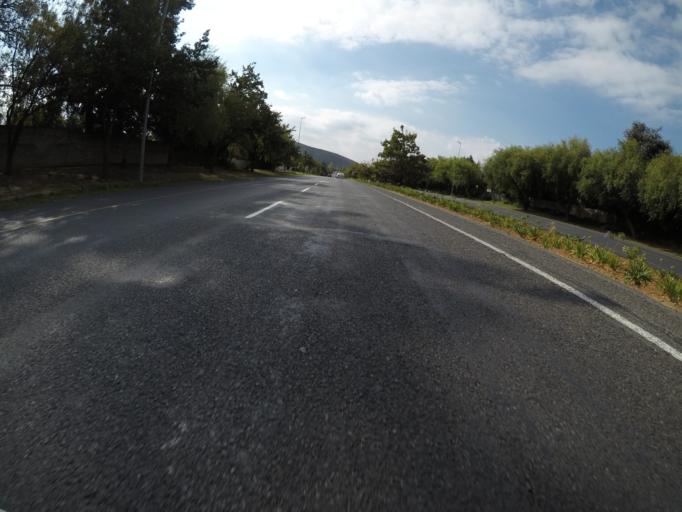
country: ZA
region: Western Cape
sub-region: Cape Winelands District Municipality
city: Stellenbosch
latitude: -33.9518
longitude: 18.8554
